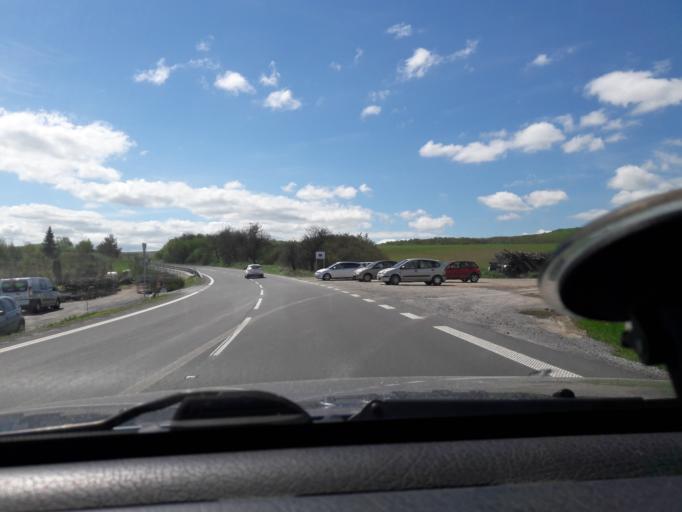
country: SK
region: Banskobystricky
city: Krupina
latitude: 48.4636
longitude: 19.0983
